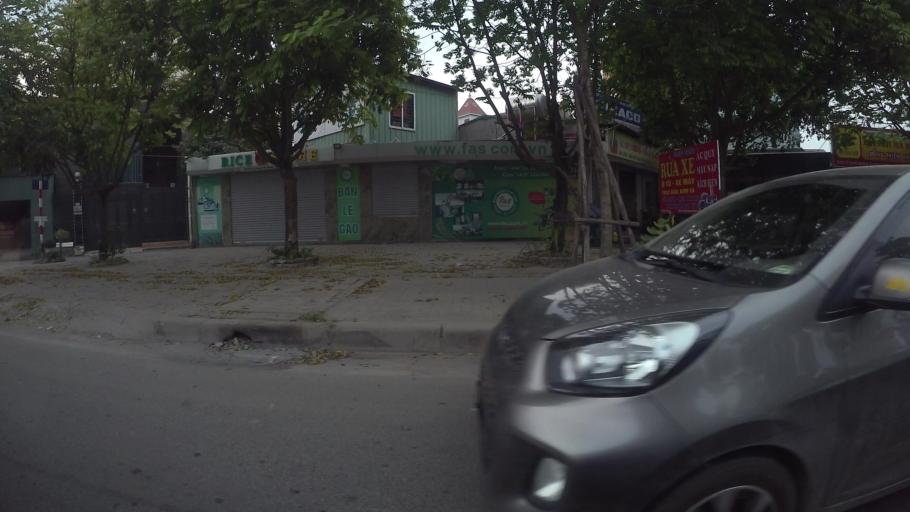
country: VN
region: Ha Noi
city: Trau Quy
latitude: 21.0053
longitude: 105.9116
